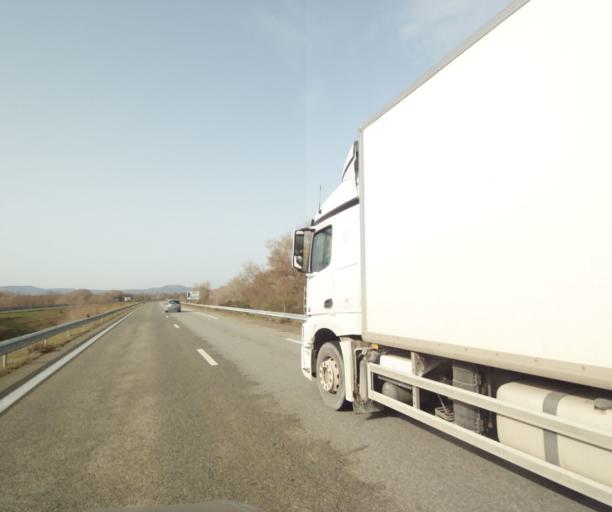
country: FR
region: Provence-Alpes-Cote d'Azur
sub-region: Departement des Bouches-du-Rhone
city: Meyrargues
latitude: 43.6572
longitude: 5.5324
